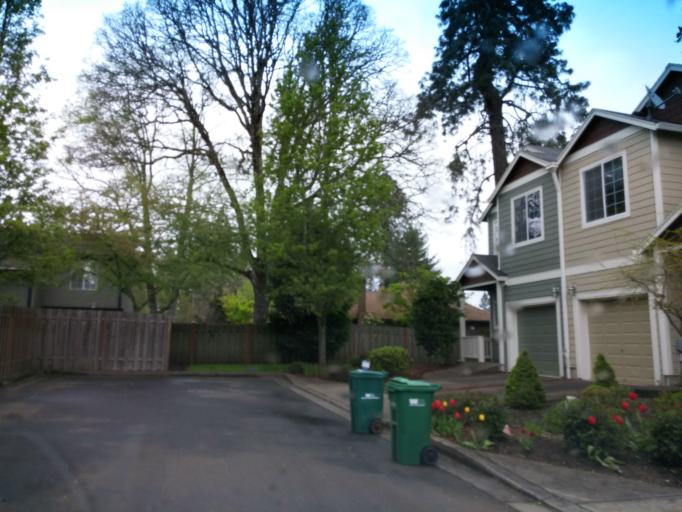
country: US
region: Oregon
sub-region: Washington County
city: Cedar Mill
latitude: 45.5166
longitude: -122.8291
